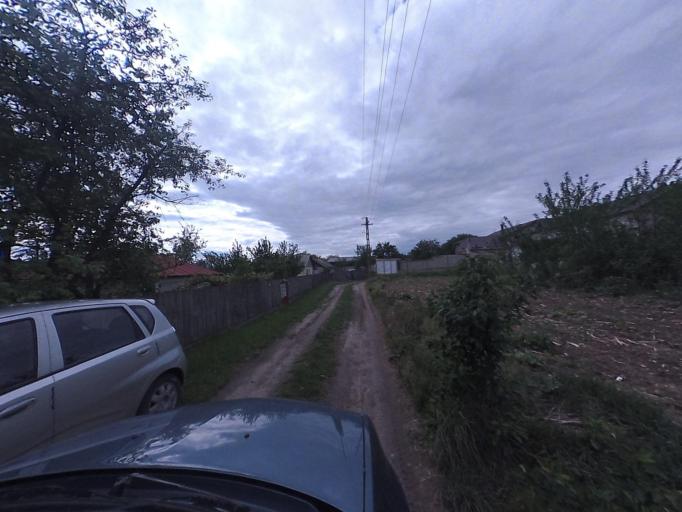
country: RO
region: Neamt
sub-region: Comuna Dulcesti
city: Dulcesti
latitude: 46.9609
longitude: 26.7950
